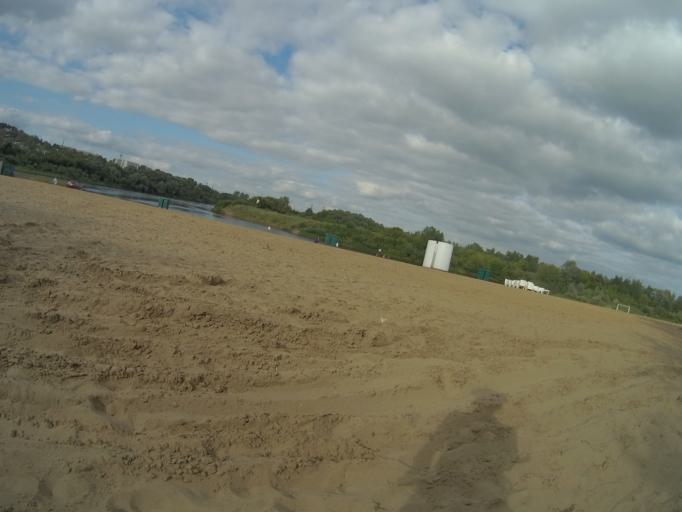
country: RU
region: Vladimir
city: Vladimir
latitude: 56.1241
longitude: 40.4169
